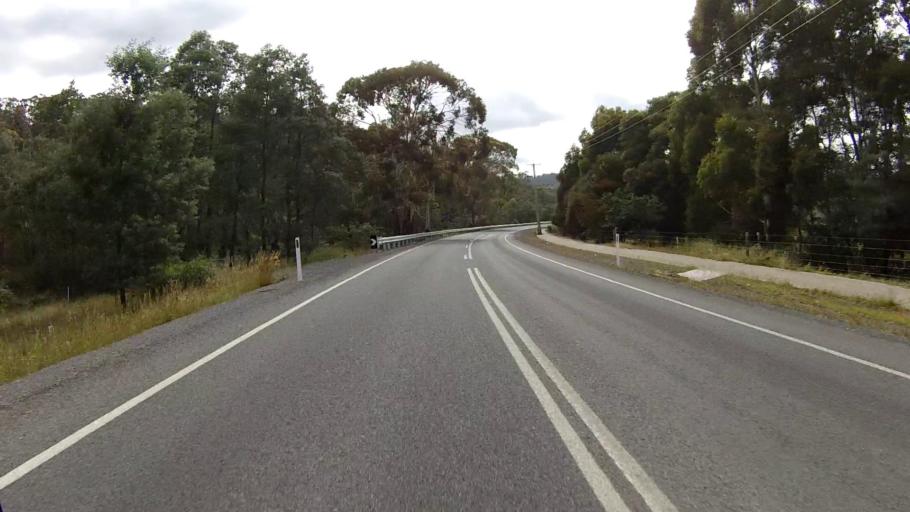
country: AU
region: Tasmania
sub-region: Glenorchy
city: Lutana
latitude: -42.8083
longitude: 147.3386
